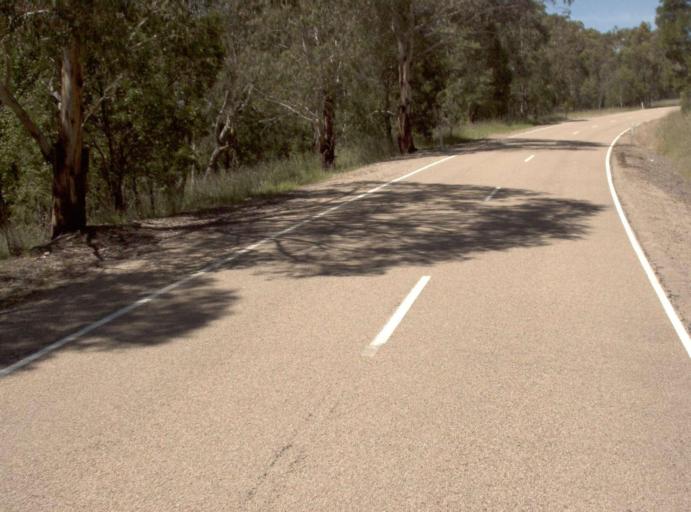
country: AU
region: Victoria
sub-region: East Gippsland
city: Lakes Entrance
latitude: -37.2104
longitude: 148.2697
